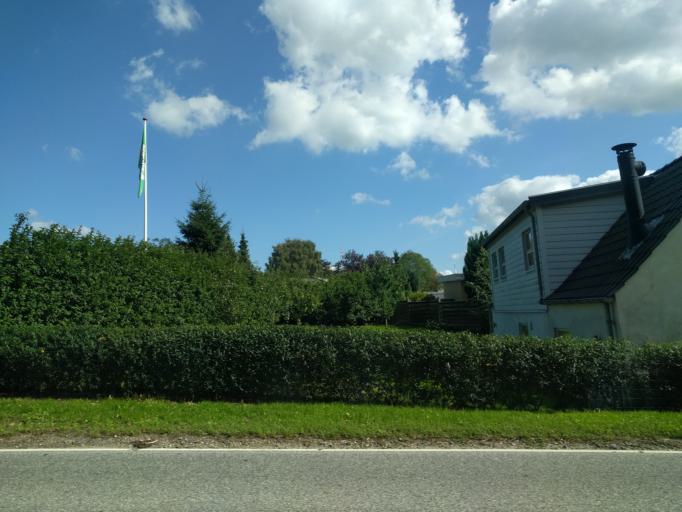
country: DK
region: Central Jutland
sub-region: Skive Kommune
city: Skive
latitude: 56.5872
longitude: 9.0295
